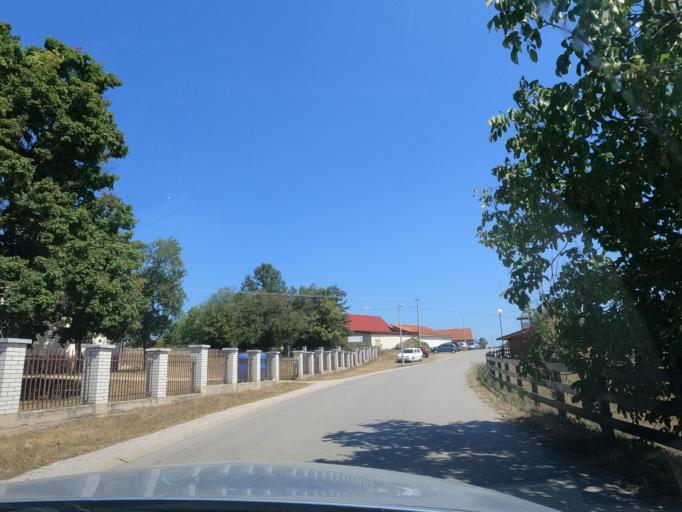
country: RS
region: Central Serbia
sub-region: Zlatiborski Okrug
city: Cajetina
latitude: 43.7889
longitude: 19.7675
